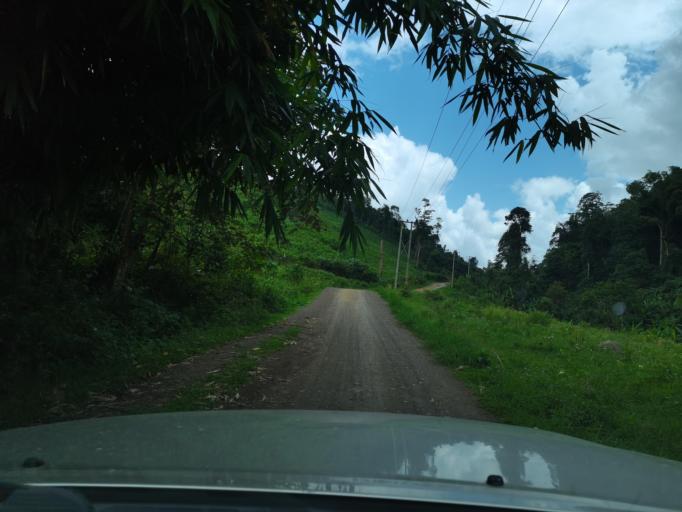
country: LA
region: Loungnamtha
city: Muang Long
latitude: 20.7797
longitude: 101.0163
